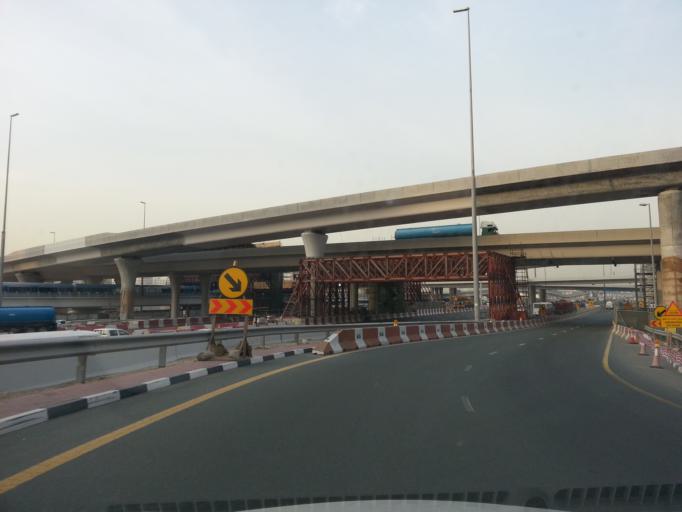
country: AE
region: Dubai
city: Dubai
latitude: 25.0665
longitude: 55.1336
